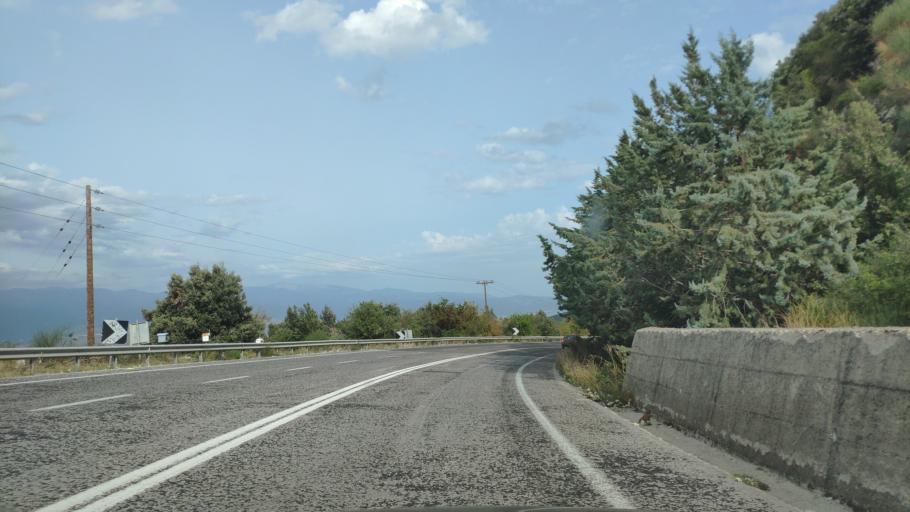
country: GR
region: Central Greece
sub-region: Nomos Fthiotidos
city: Anthili
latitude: 38.7754
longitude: 22.4683
